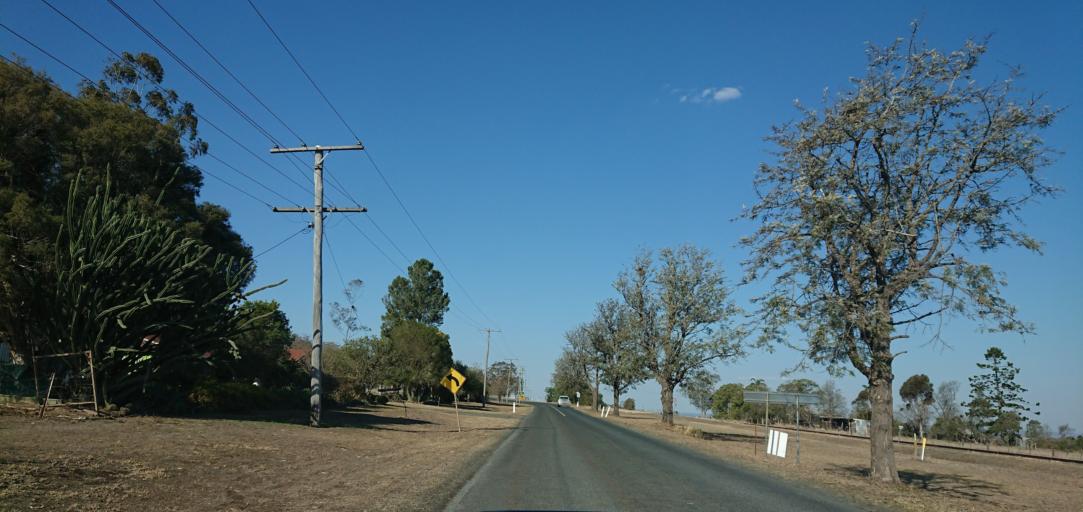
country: AU
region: Queensland
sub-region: Toowoomba
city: Westbrook
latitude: -27.6781
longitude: 151.7178
